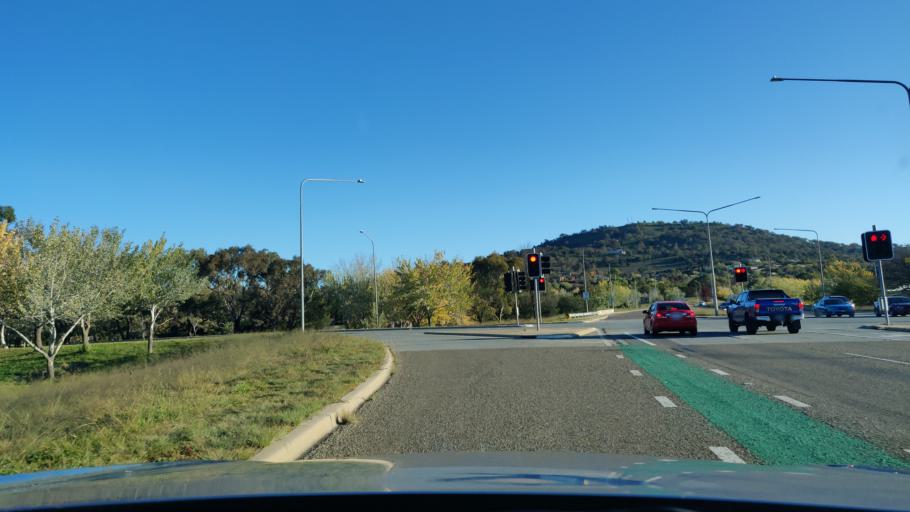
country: AU
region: Australian Capital Territory
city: Macarthur
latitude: -35.4409
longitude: 149.1221
